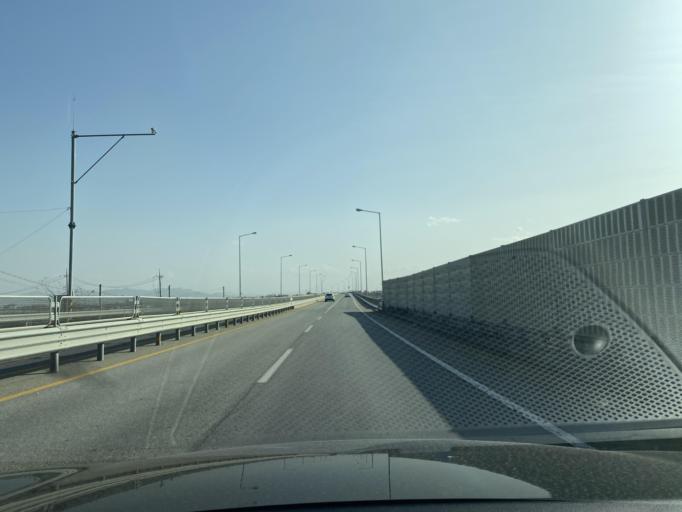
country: KR
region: Chungcheongnam-do
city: Yesan
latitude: 36.6922
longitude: 126.7334
